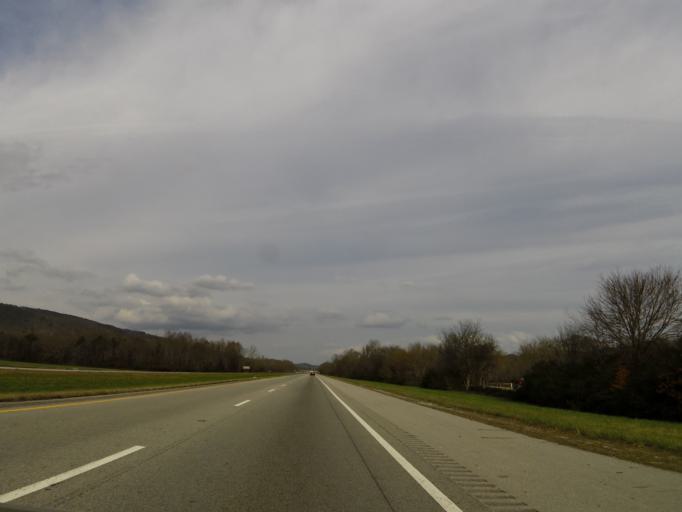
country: US
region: Tennessee
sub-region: Hamilton County
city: Soddy-Daisy
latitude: 35.2201
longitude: -85.2105
